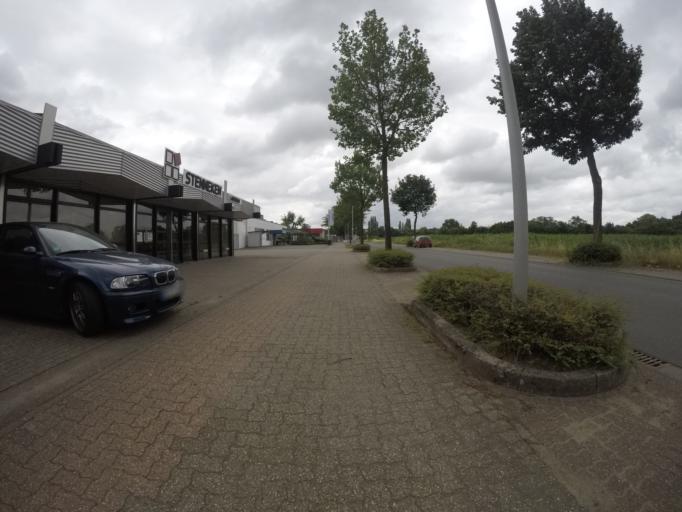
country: DE
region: North Rhine-Westphalia
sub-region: Regierungsbezirk Dusseldorf
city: Bocholt
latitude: 51.8073
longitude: 6.6038
